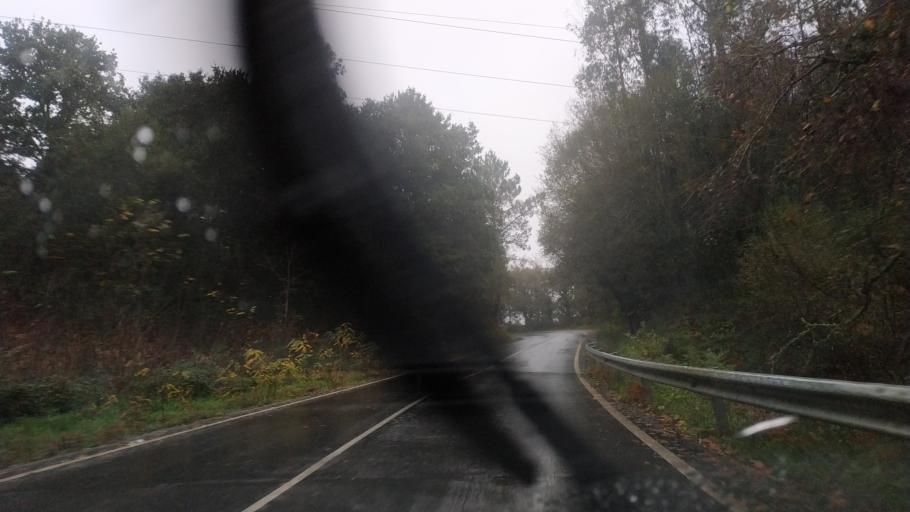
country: ES
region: Galicia
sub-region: Provincia da Coruna
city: Negreira
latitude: 42.9079
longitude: -8.7476
